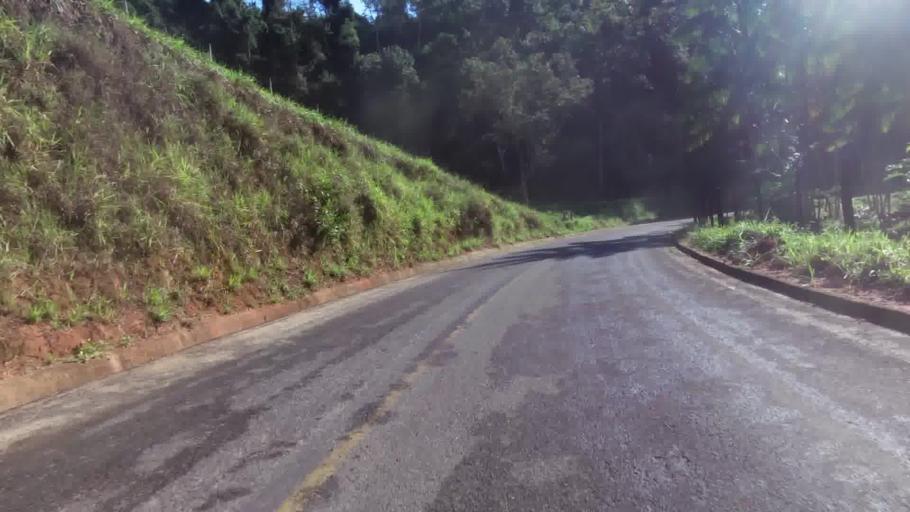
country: BR
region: Espirito Santo
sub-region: Alfredo Chaves
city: Alfredo Chaves
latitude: -20.6839
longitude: -40.7747
